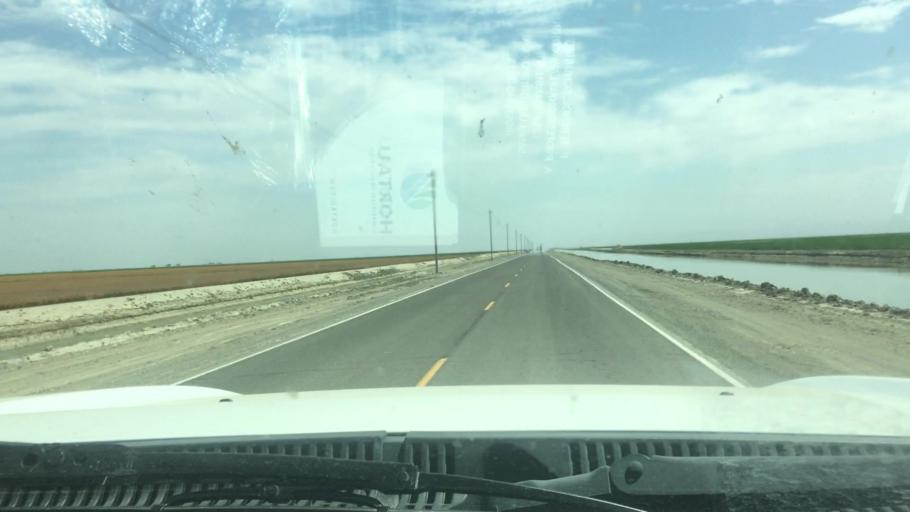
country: US
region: California
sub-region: Tulare County
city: Alpaugh
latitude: 35.9037
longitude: -119.5733
